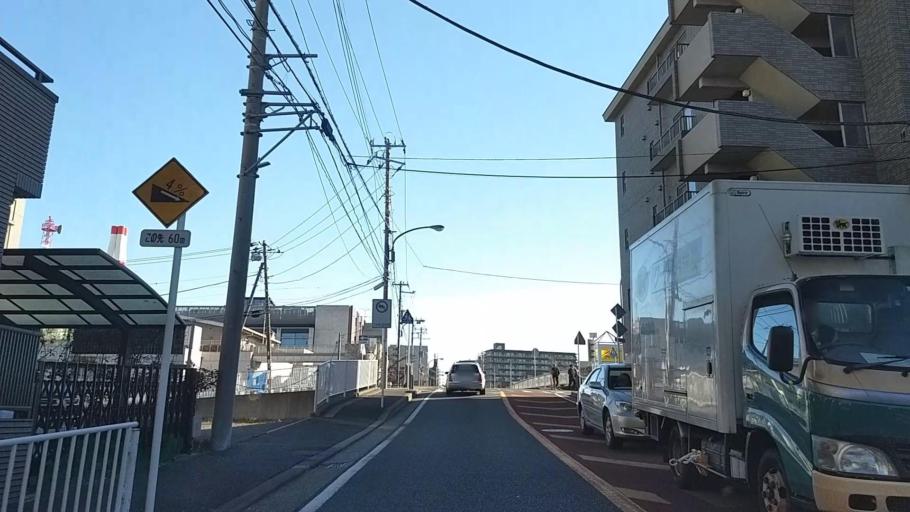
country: JP
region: Kanagawa
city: Yokohama
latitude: 35.4589
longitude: 139.6119
